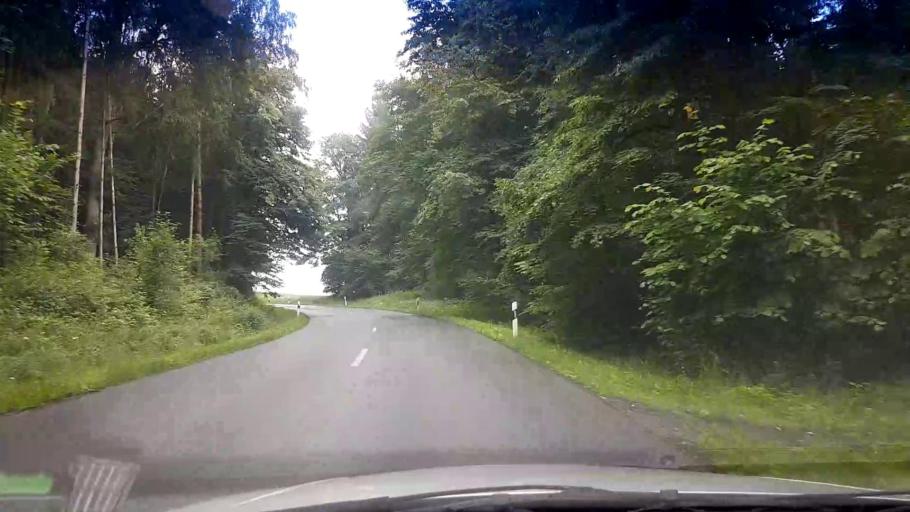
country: DE
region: Bavaria
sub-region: Upper Franconia
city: Kasendorf
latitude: 50.0711
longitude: 11.3333
